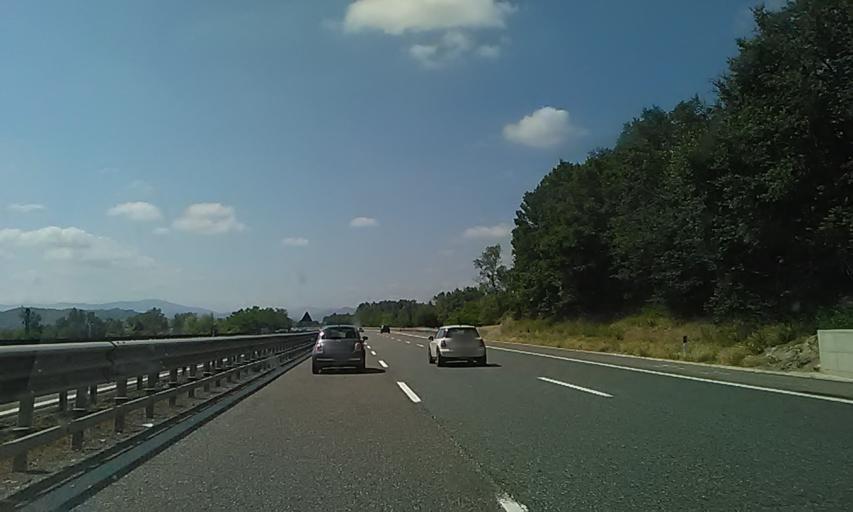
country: IT
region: Piedmont
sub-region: Provincia di Alessandria
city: Capriata d'Orba
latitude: 44.7187
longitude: 8.6670
